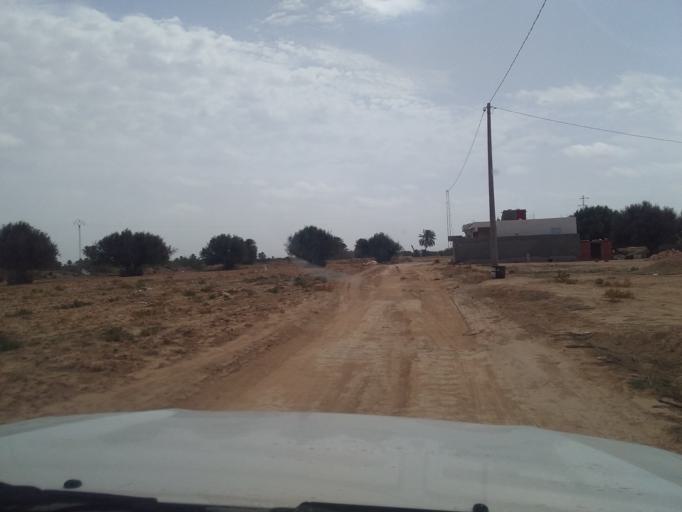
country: TN
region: Qabis
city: Matmata
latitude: 33.6195
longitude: 10.2671
